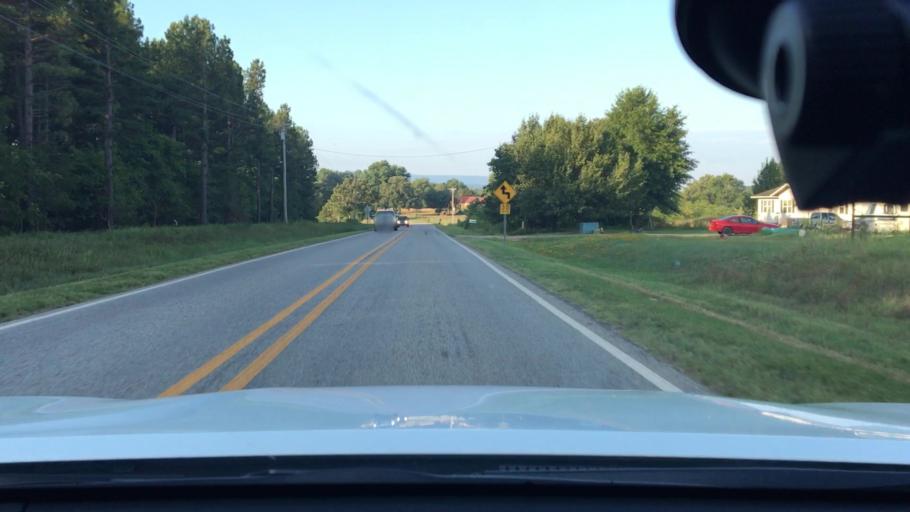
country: US
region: Arkansas
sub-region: Johnson County
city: Coal Hill
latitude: 35.3449
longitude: -93.5955
